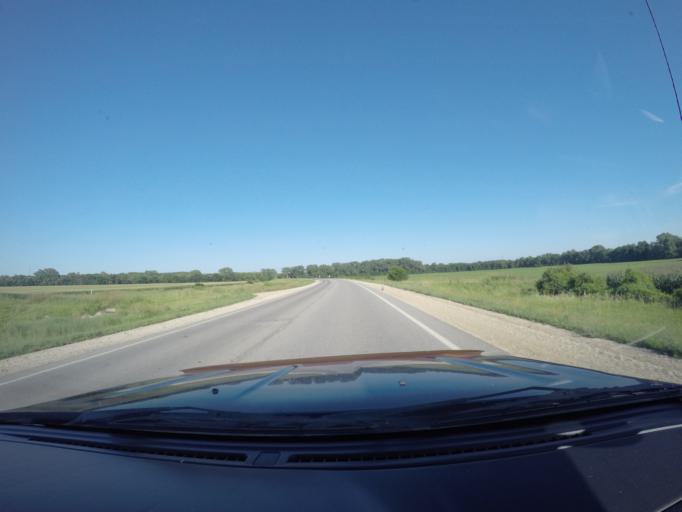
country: US
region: Kansas
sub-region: Jefferson County
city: Oskaloosa
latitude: 39.0815
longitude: -95.4038
